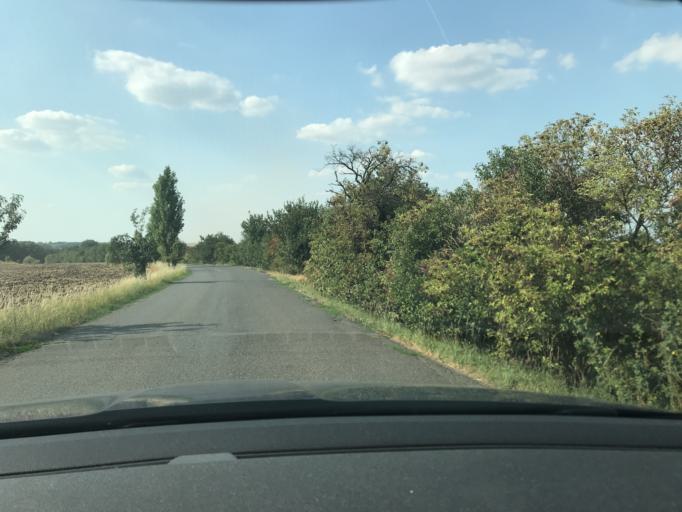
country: CZ
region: Central Bohemia
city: Kralupy nad Vltavou
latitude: 50.2305
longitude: 14.3166
